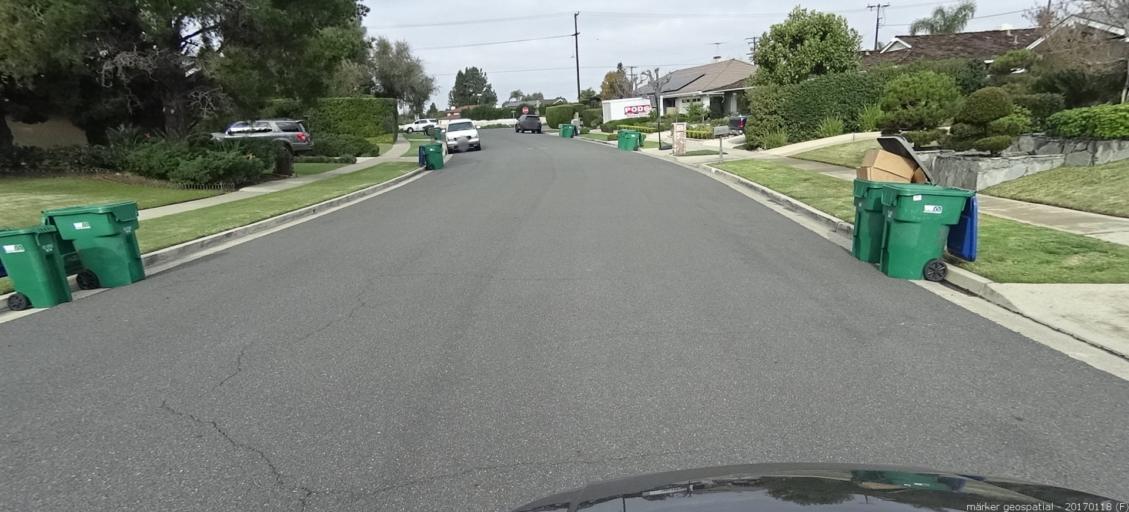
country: US
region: California
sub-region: Orange County
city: North Tustin
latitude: 33.7590
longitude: -117.8003
